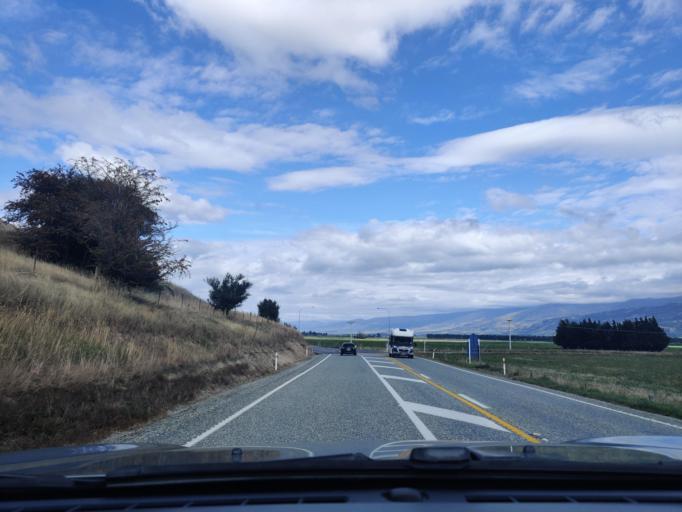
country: NZ
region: Otago
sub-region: Queenstown-Lakes District
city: Wanaka
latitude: -44.8417
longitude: 169.4017
